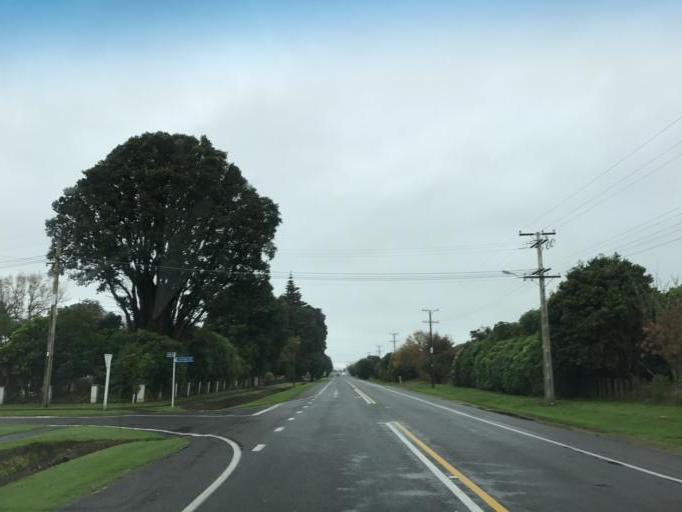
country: NZ
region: Taranaki
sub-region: South Taranaki District
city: Patea
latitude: -39.7647
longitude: 174.6250
